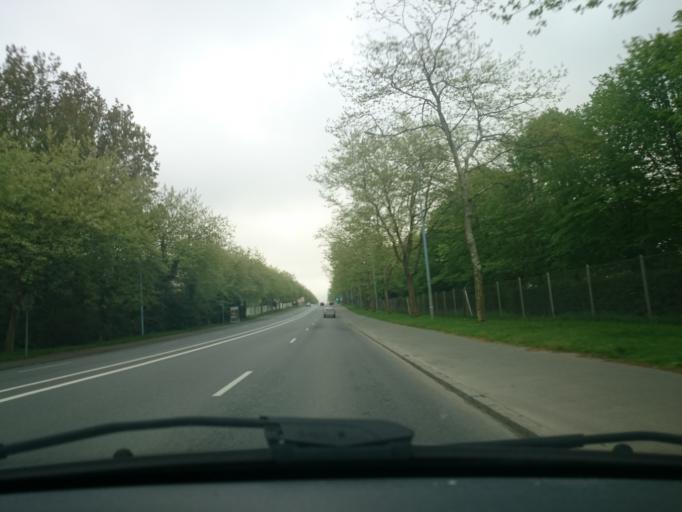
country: FR
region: Brittany
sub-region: Departement du Finistere
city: Bohars
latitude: 48.4128
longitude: -4.5059
